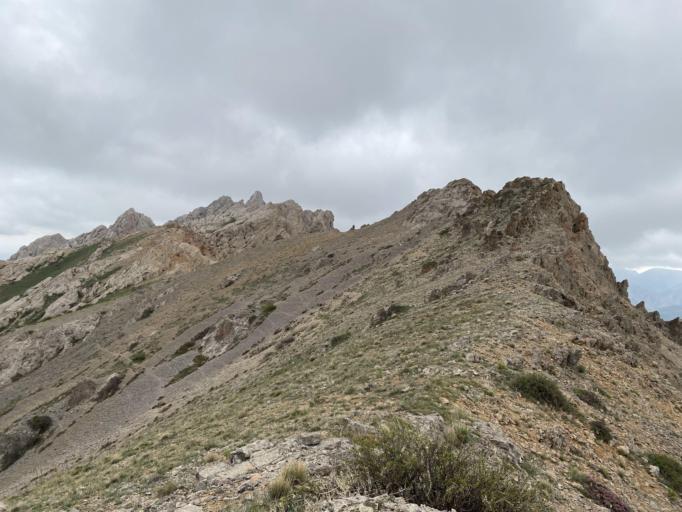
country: KZ
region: Ongtustik Qazaqstan
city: Ashchysay
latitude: 43.7476
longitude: 68.8293
